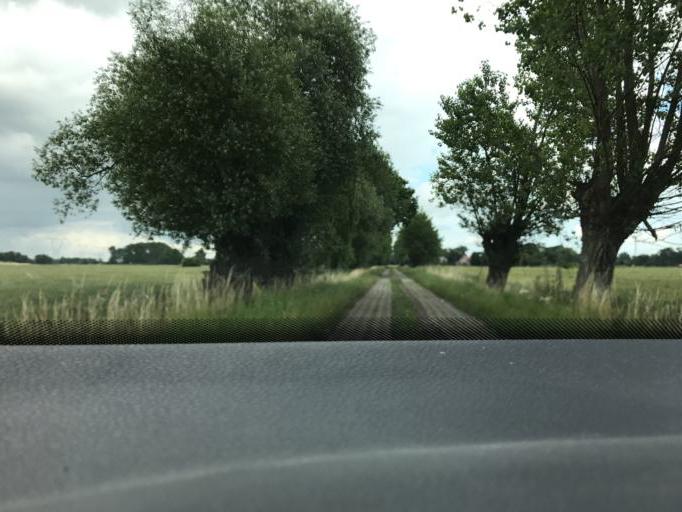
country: PL
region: Pomeranian Voivodeship
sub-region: Gdansk
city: Gdansk
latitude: 54.3100
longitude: 18.7201
